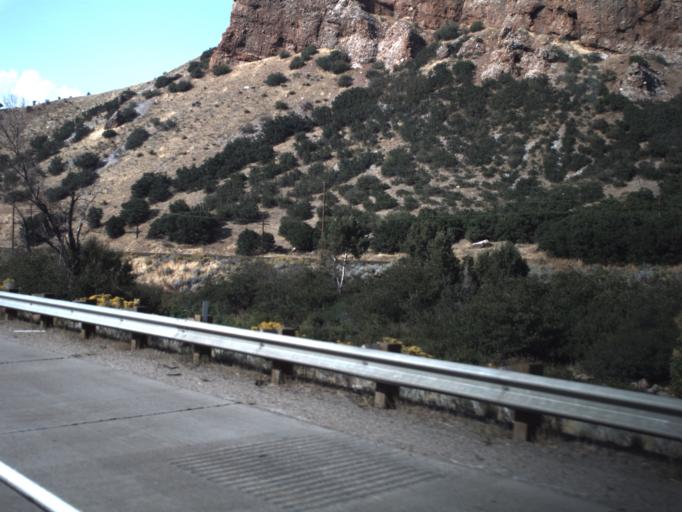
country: US
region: Utah
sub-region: Morgan County
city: Morgan
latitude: 41.0563
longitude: -111.5318
